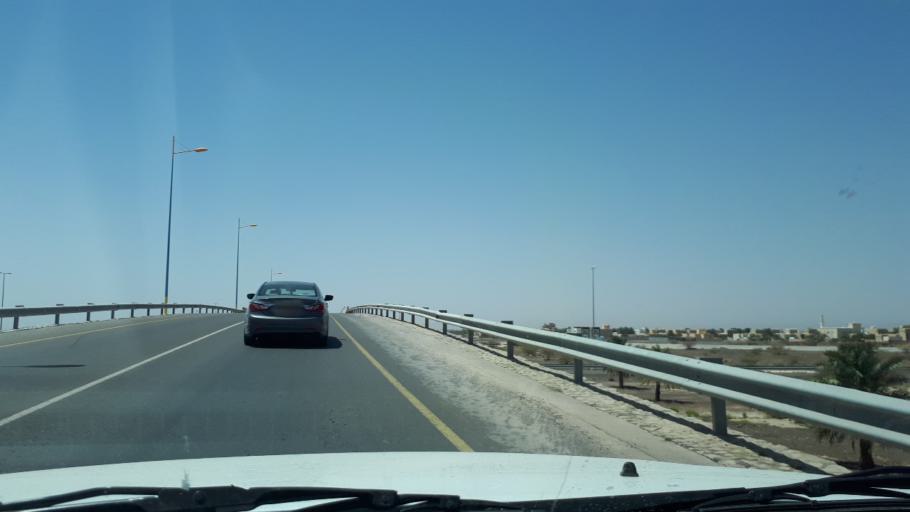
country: OM
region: Muhafazat ad Dakhiliyah
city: Bahla'
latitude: 22.9286
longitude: 57.2565
